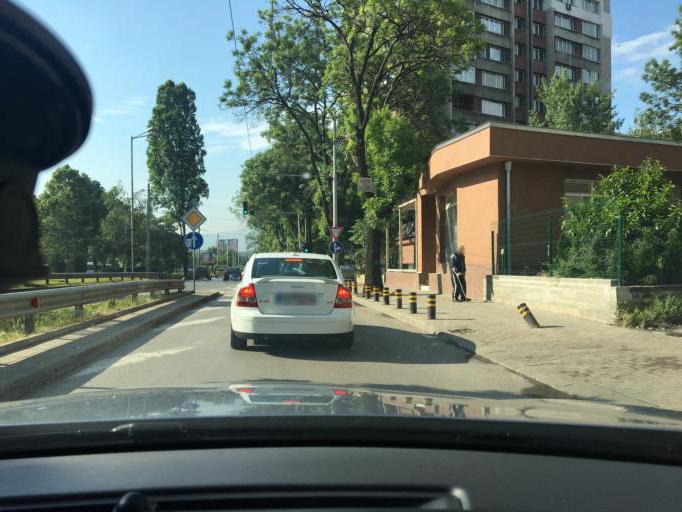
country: BG
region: Sofia-Capital
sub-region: Stolichna Obshtina
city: Sofia
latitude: 42.6827
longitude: 23.3013
